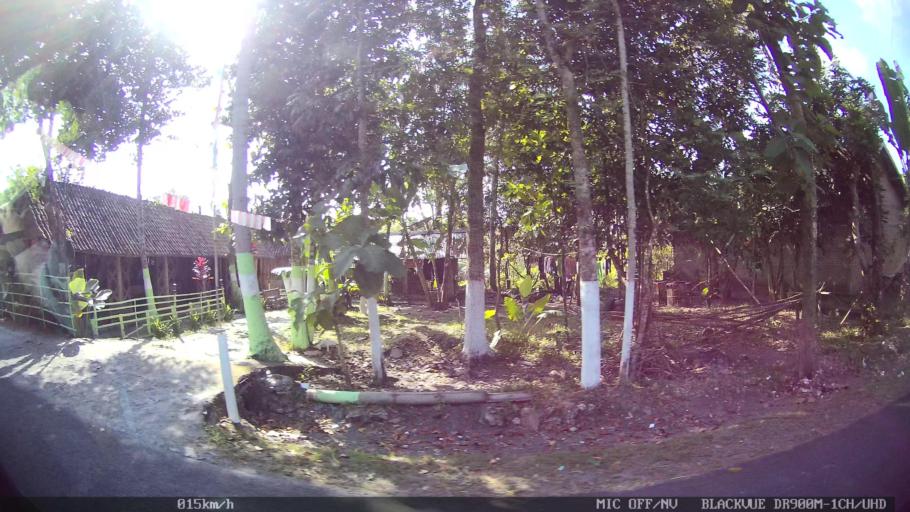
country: ID
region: Daerah Istimewa Yogyakarta
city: Kasihan
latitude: -7.8195
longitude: 110.2936
